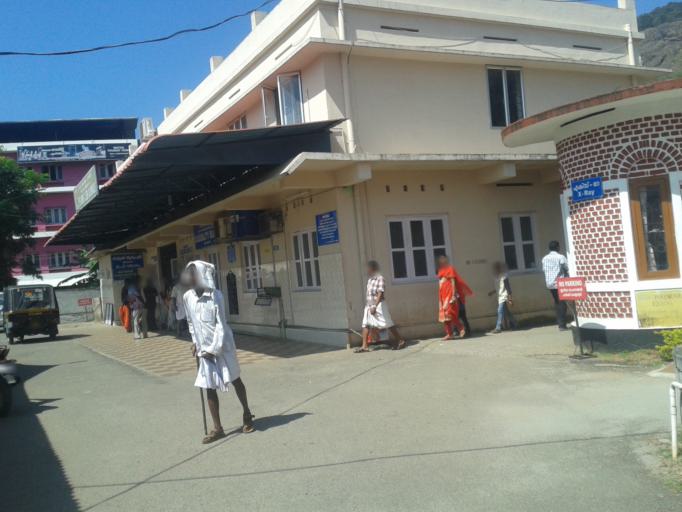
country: IN
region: Kerala
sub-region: Idukki
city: Munnar
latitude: 10.0140
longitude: 76.9552
